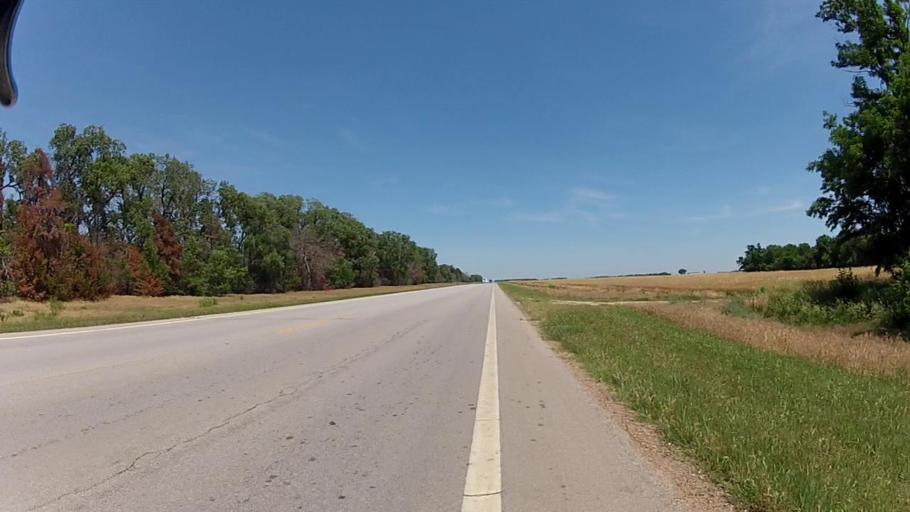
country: US
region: Kansas
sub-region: Harper County
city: Harper
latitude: 37.2390
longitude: -98.1605
